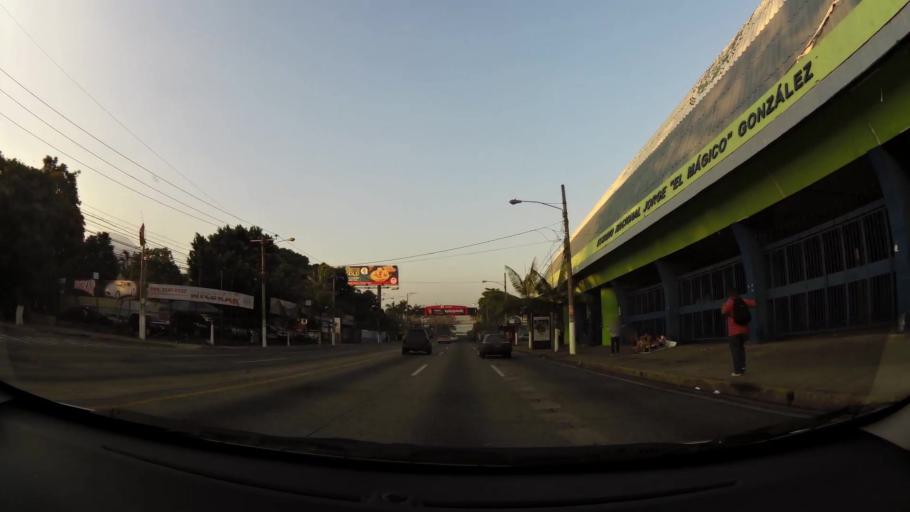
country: SV
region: San Salvador
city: San Salvador
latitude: 13.6983
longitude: -89.2164
